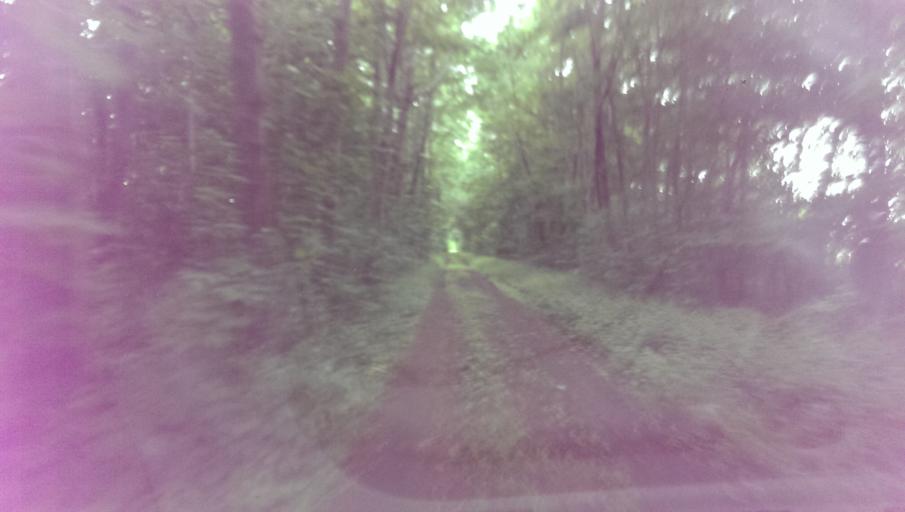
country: DK
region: South Denmark
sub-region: Esbjerg Kommune
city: Bramming
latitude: 55.4427
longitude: 8.7151
